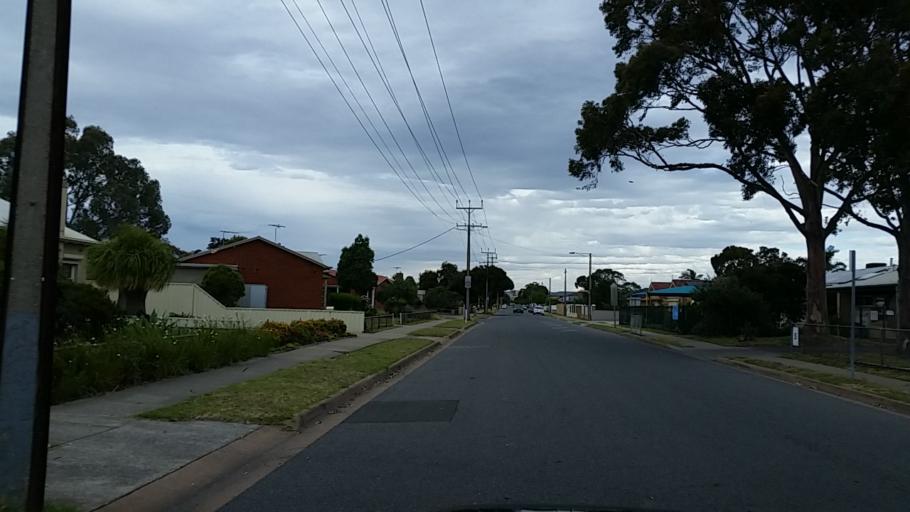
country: AU
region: South Australia
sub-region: Charles Sturt
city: Royal Park
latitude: -34.8848
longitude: 138.5078
